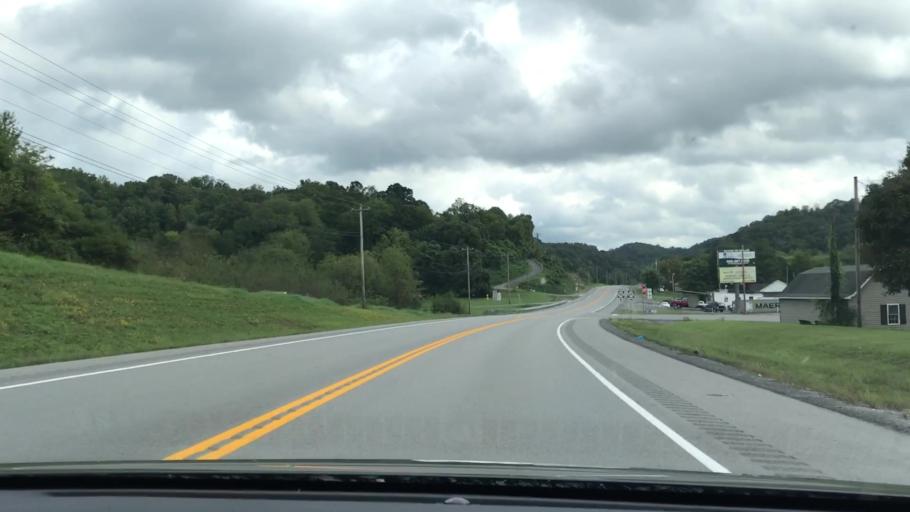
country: US
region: Kentucky
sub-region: Cumberland County
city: Burkesville
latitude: 36.7938
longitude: -85.4054
